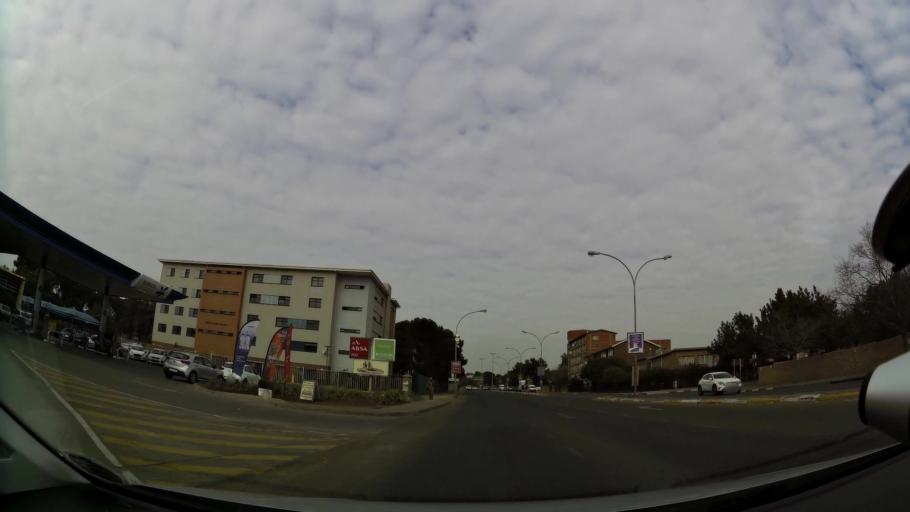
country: ZA
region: Orange Free State
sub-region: Mangaung Metropolitan Municipality
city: Bloemfontein
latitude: -29.1222
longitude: 26.2120
